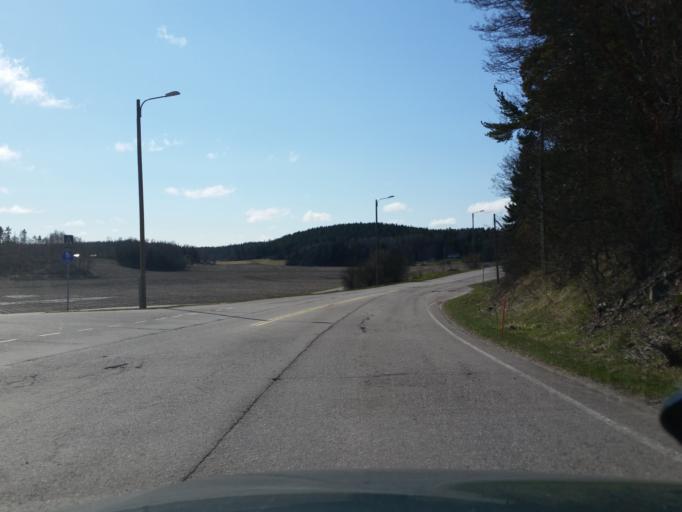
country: FI
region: Uusimaa
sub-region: Helsinki
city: Vihti
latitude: 60.4169
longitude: 24.2901
